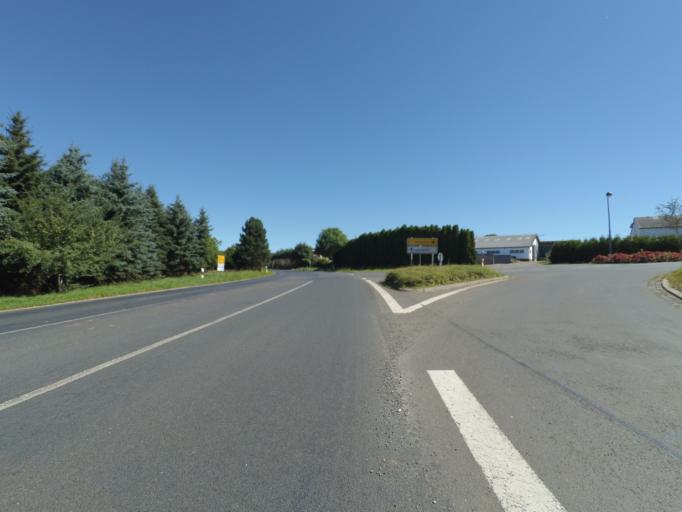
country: DE
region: Rheinland-Pfalz
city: Wiesbaum
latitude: 50.3426
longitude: 6.6713
